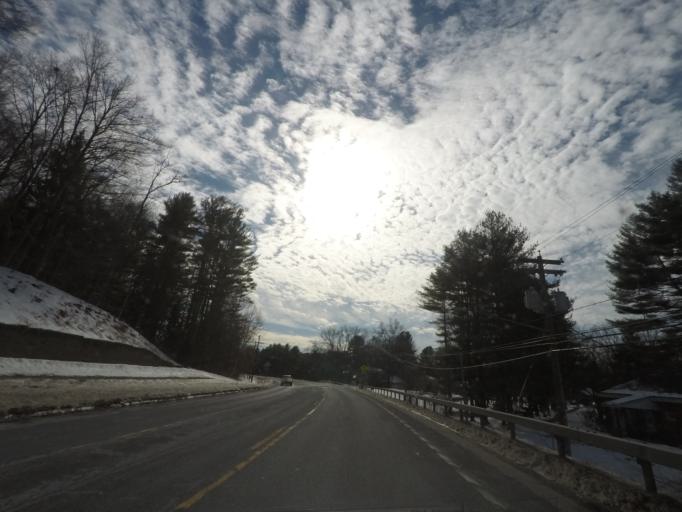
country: US
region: New York
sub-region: Albany County
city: Westmere
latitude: 42.6900
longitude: -73.9000
